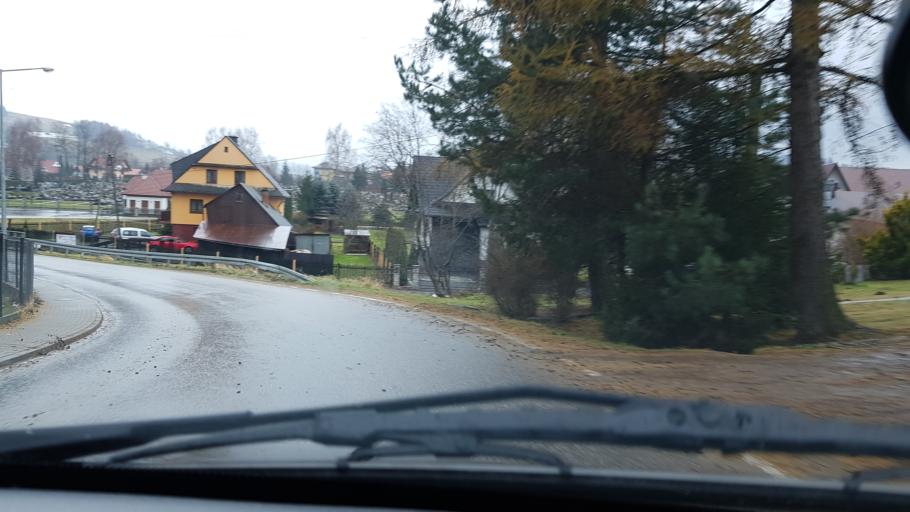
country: PL
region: Lesser Poland Voivodeship
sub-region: Powiat nowotarski
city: Raba Wyzna
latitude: 49.5698
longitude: 19.8732
